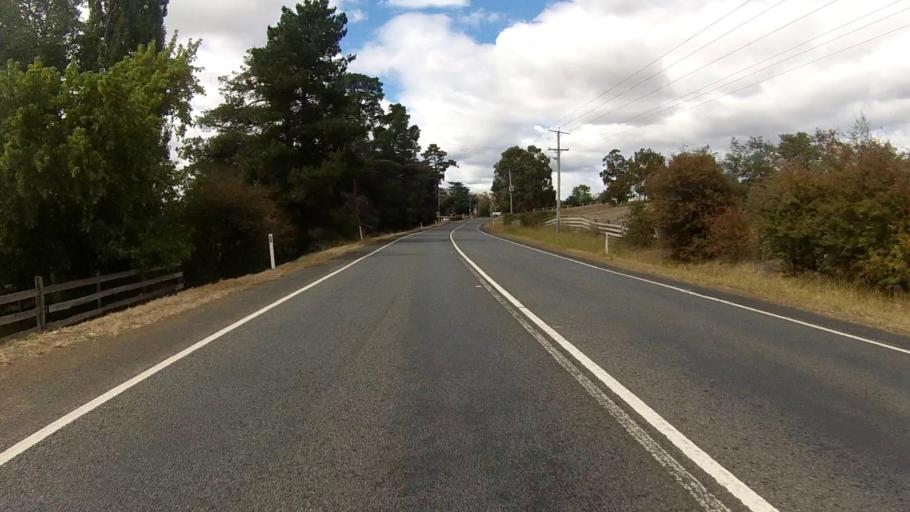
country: AU
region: Tasmania
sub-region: Brighton
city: Bridgewater
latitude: -42.6781
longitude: 147.2645
